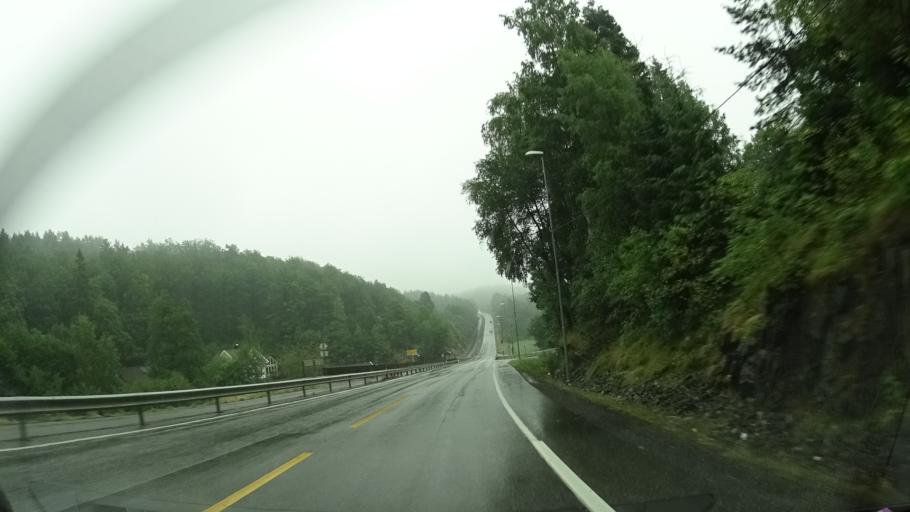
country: NO
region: Aust-Agder
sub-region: Lillesand
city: Lillesand
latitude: 58.2386
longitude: 8.3358
